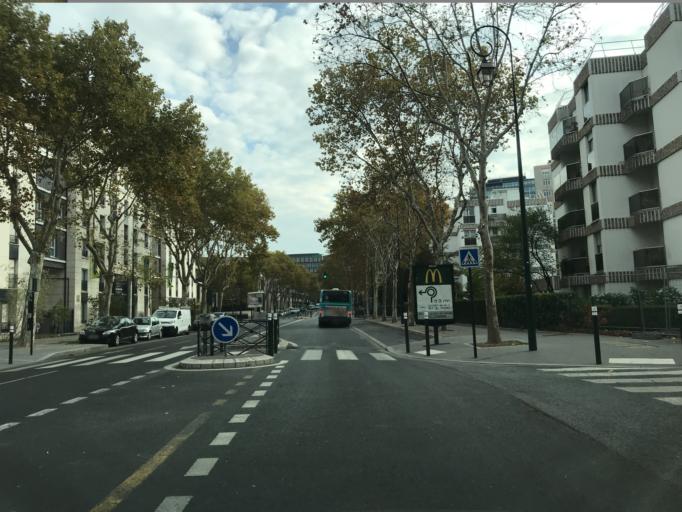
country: FR
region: Ile-de-France
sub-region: Departement des Hauts-de-Seine
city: La Garenne-Colombes
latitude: 48.9052
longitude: 2.2345
